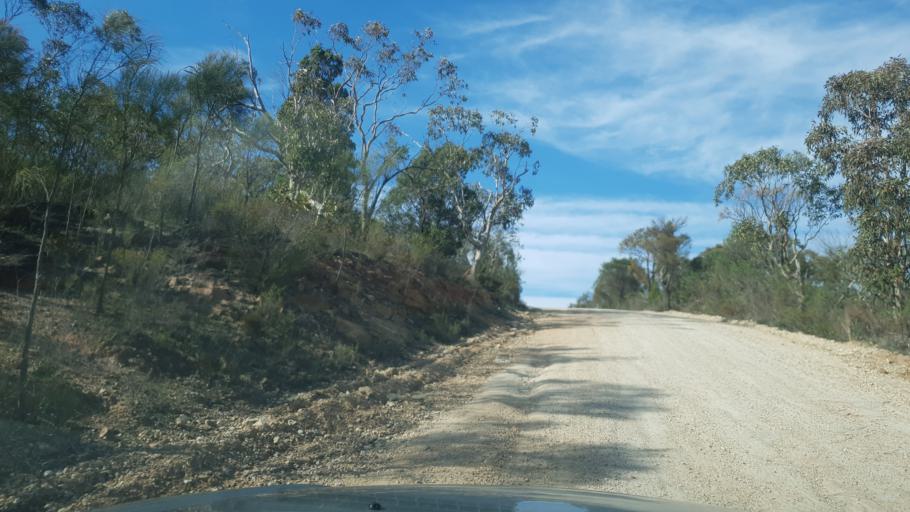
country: AU
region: South Australia
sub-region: Playford
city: One Tree Hill
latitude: -34.6540
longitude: 138.8216
